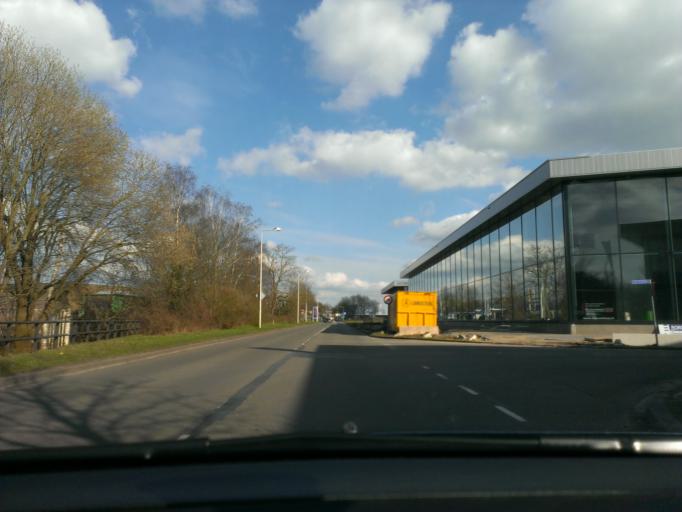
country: NL
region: Overijssel
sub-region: Gemeente Enschede
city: Enschede
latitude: 52.2189
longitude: 6.8662
